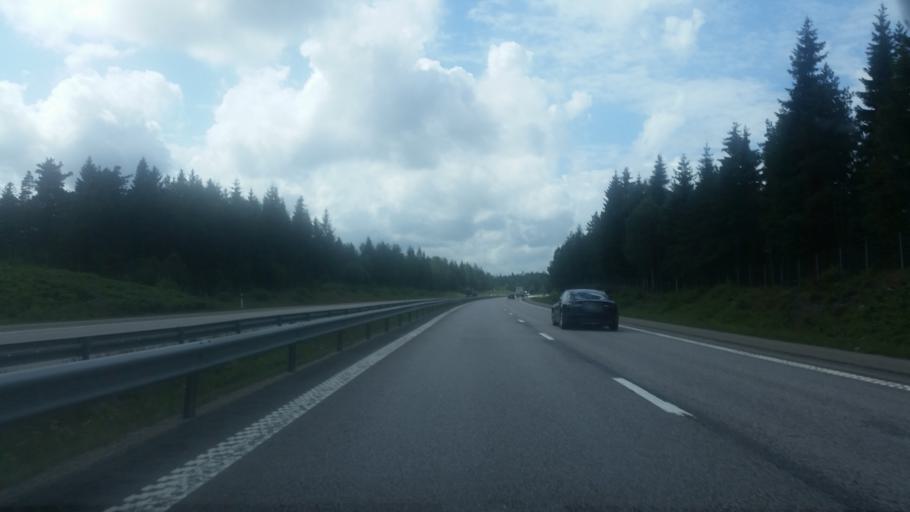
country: SE
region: Vaestra Goetaland
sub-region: Bollebygds Kommun
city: Bollebygd
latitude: 57.6726
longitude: 12.6706
